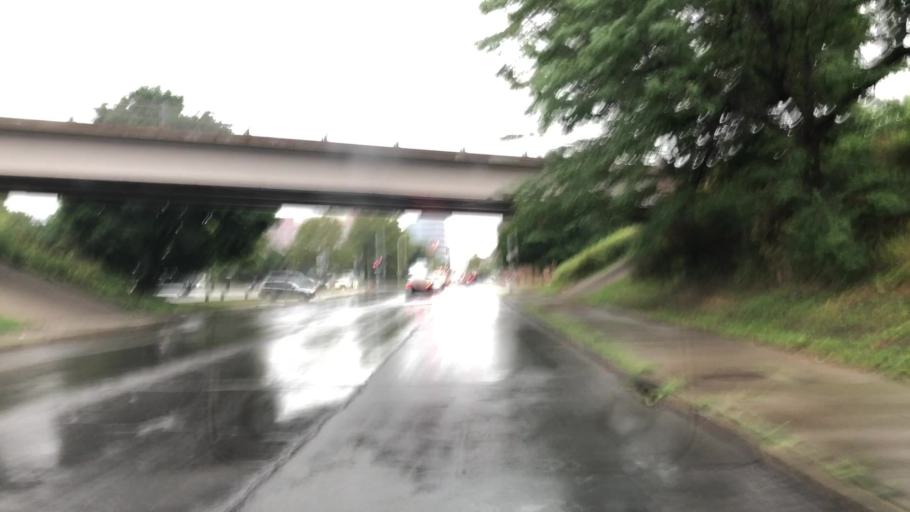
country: US
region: New York
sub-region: Erie County
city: Buffalo
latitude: 42.8932
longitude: -78.8653
